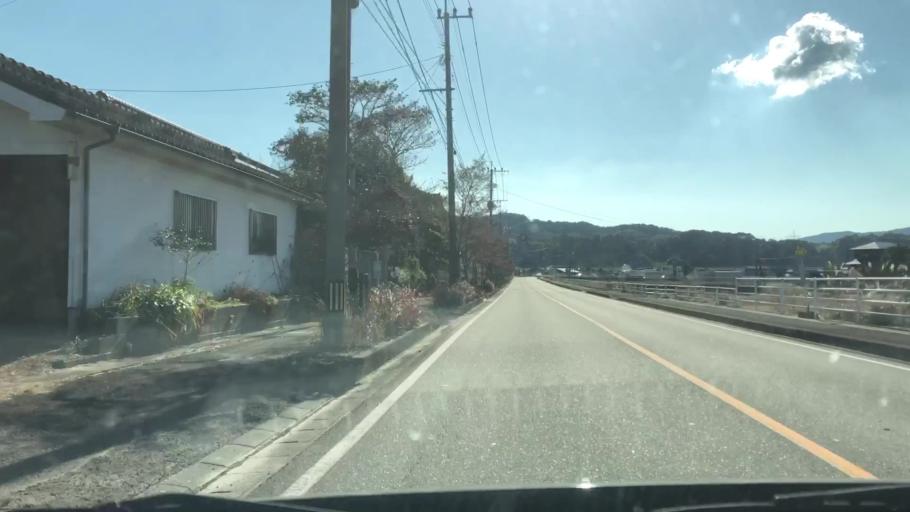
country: JP
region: Kagoshima
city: Satsumasendai
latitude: 31.8598
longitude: 130.3927
